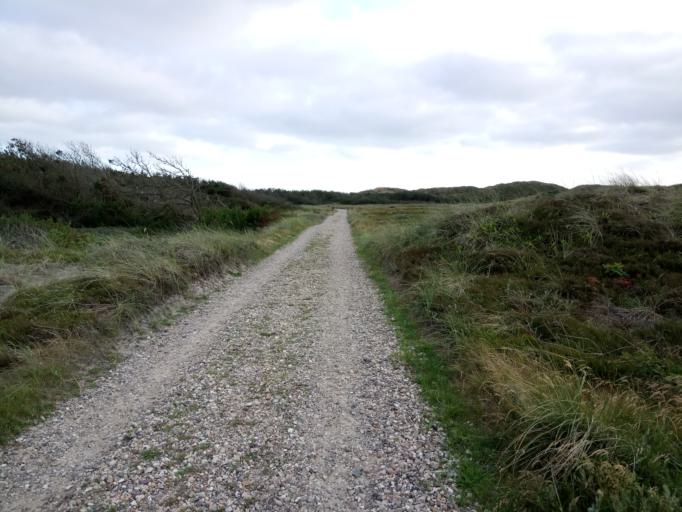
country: DK
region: Central Jutland
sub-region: Holstebro Kommune
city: Ulfborg
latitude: 56.2909
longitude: 8.1334
